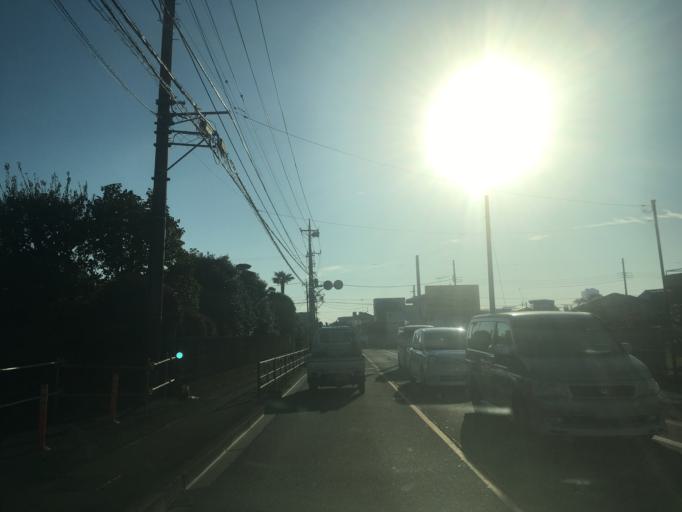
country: JP
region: Tokyo
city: Hachioji
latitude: 35.6806
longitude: 139.3551
